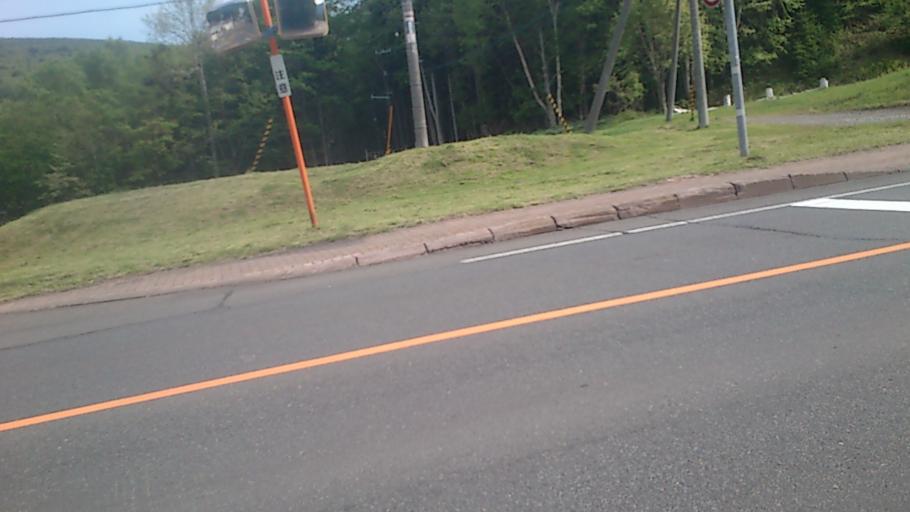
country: JP
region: Hokkaido
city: Bihoro
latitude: 43.4313
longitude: 144.0971
